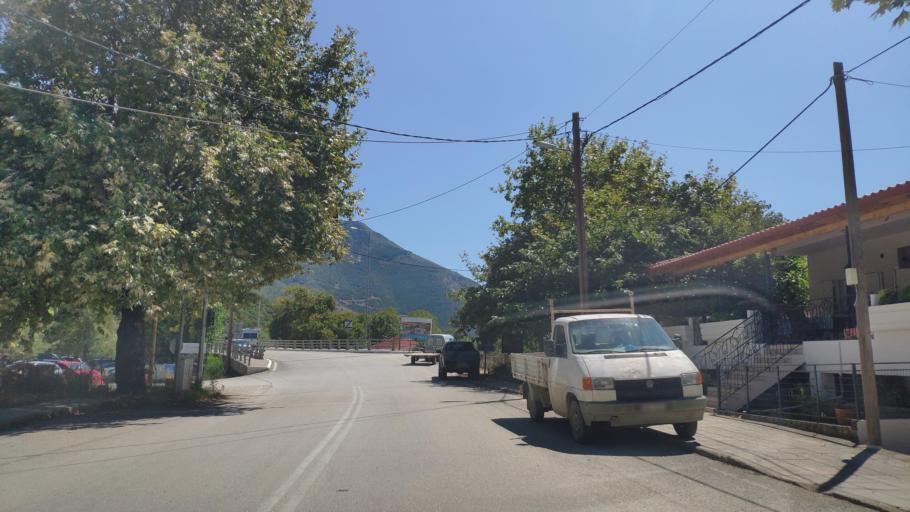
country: GR
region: Epirus
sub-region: Nomos Prevezis
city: Kanalaki
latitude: 39.3236
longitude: 20.6073
